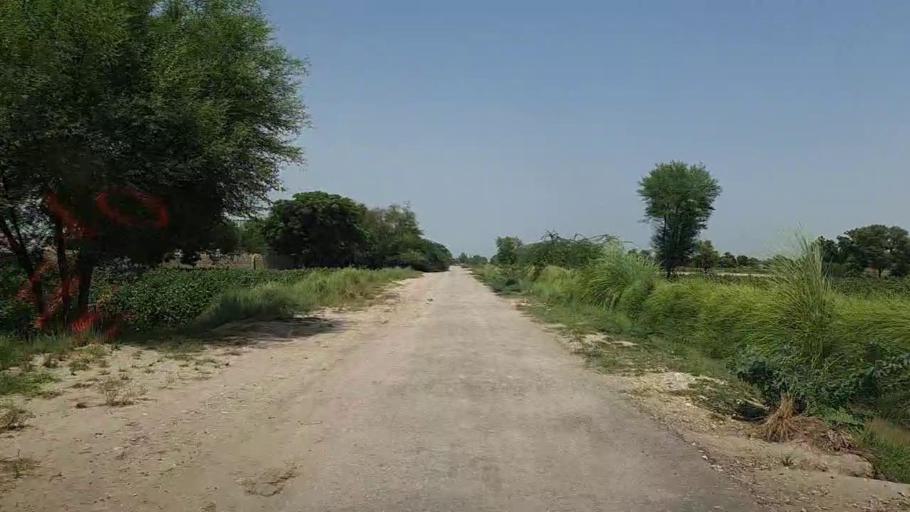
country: PK
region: Sindh
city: Pad Idan
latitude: 26.7545
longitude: 68.3171
